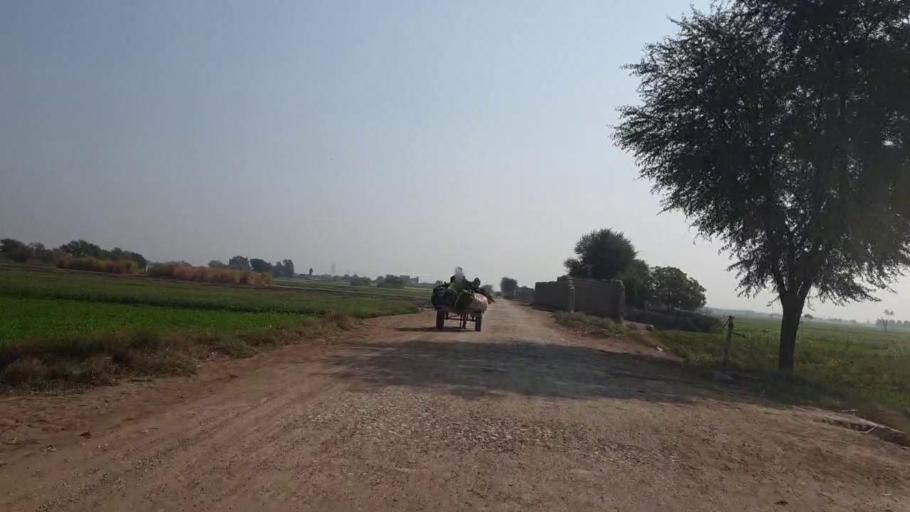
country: PK
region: Sindh
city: Bhit Shah
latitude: 25.7322
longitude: 68.5288
